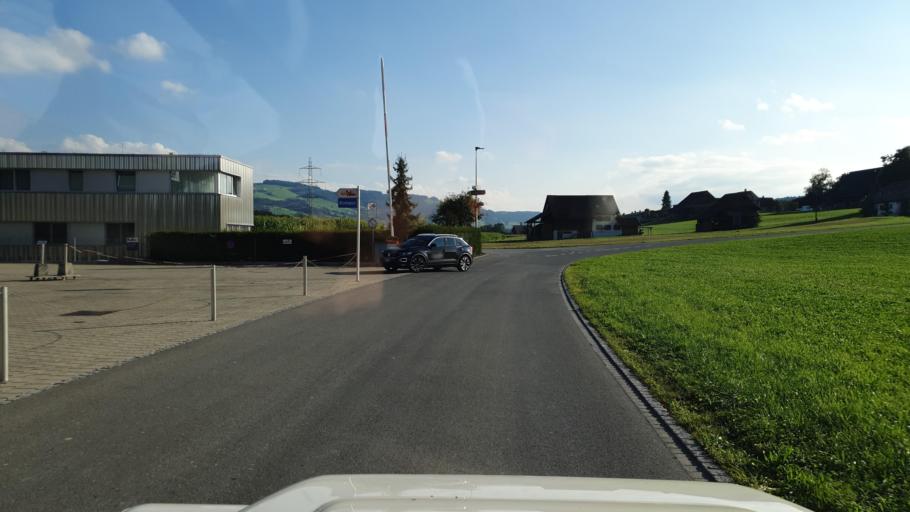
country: CH
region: Aargau
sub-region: Bezirk Muri
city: Oberruti
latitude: 47.1648
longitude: 8.4033
